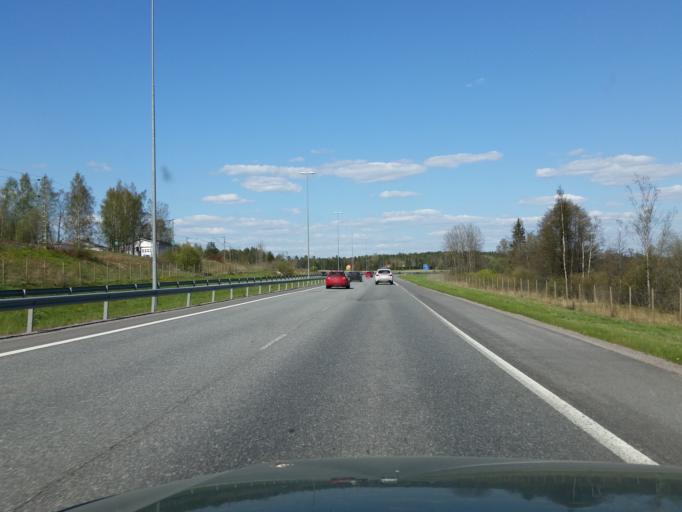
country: FI
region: Uusimaa
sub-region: Helsinki
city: Kirkkonummi
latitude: 60.1261
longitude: 24.4909
